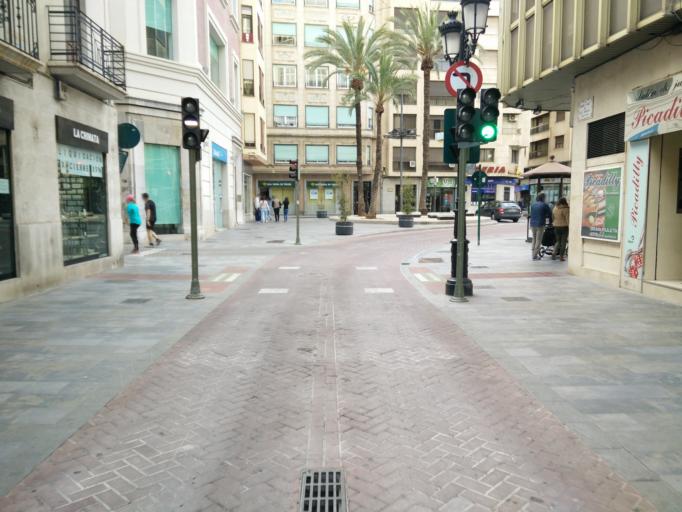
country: ES
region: Valencia
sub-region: Provincia de Castello
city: Castello de la Plana
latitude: 39.9849
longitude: -0.0404
